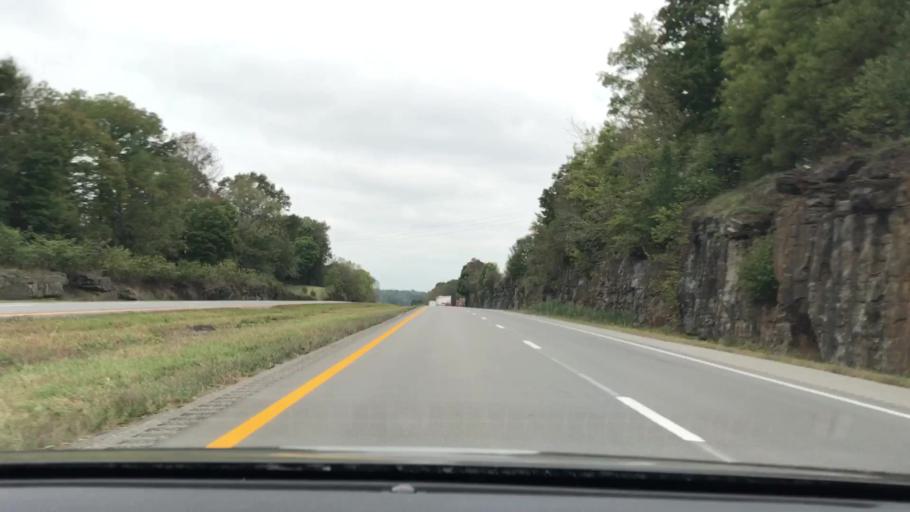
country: US
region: Kentucky
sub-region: Adair County
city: Columbia
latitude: 37.0873
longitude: -85.2663
